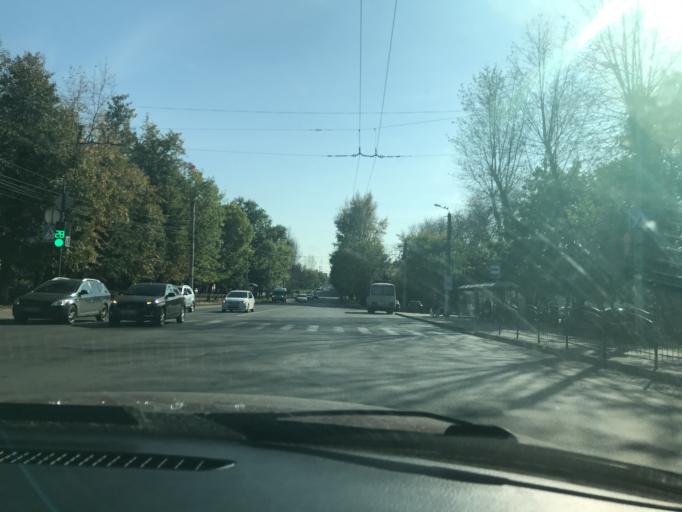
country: RU
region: Kaluga
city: Kaluga
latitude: 54.5388
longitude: 36.2697
